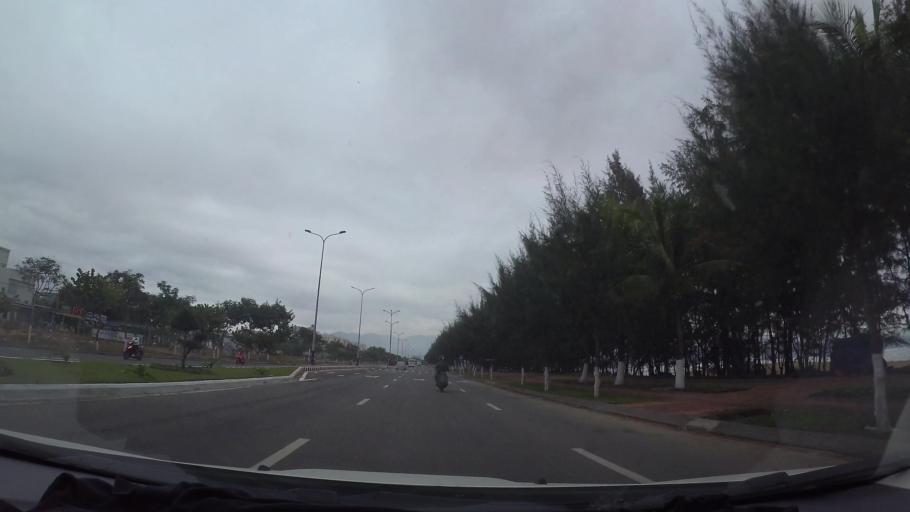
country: VN
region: Da Nang
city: Lien Chieu
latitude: 16.1048
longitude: 108.1369
